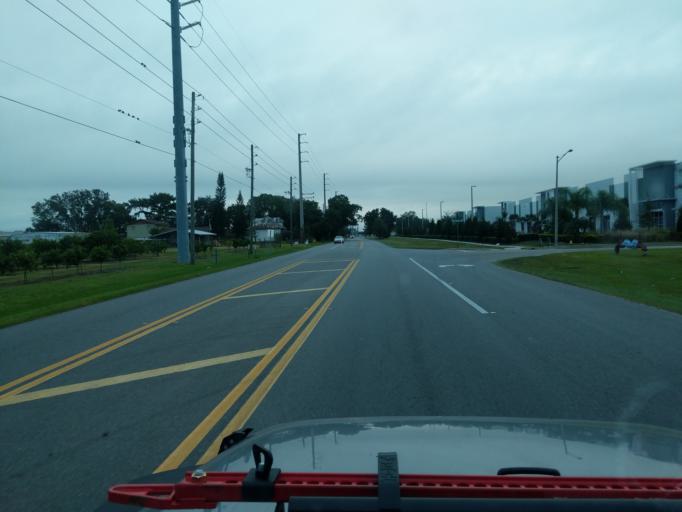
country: US
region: Florida
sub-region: Orange County
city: Winter Garden
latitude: 28.5585
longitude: -81.5707
